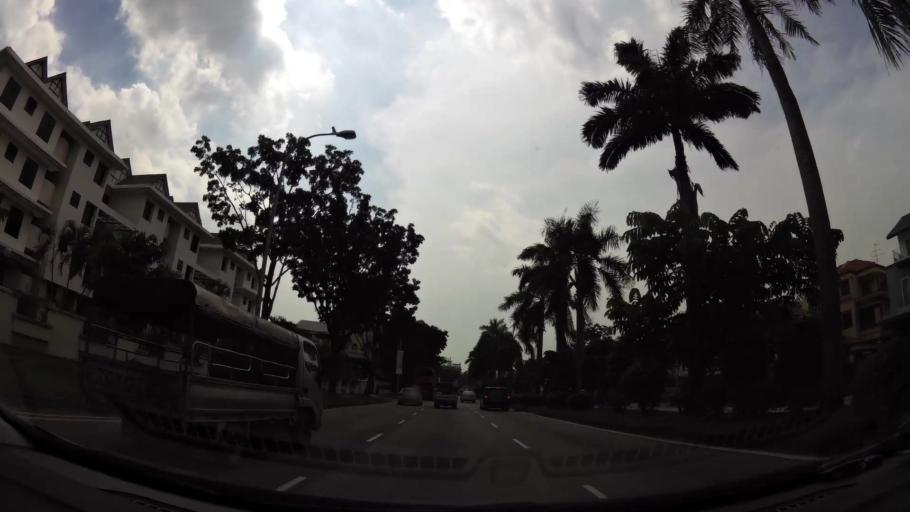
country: SG
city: Singapore
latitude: 1.3120
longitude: 103.9073
